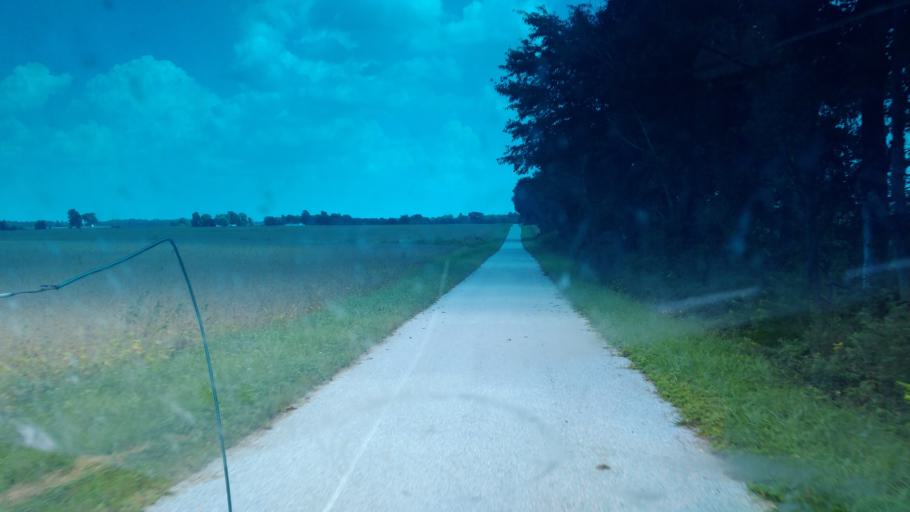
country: US
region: Ohio
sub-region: Hardin County
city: Ada
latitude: 40.7148
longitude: -83.7798
